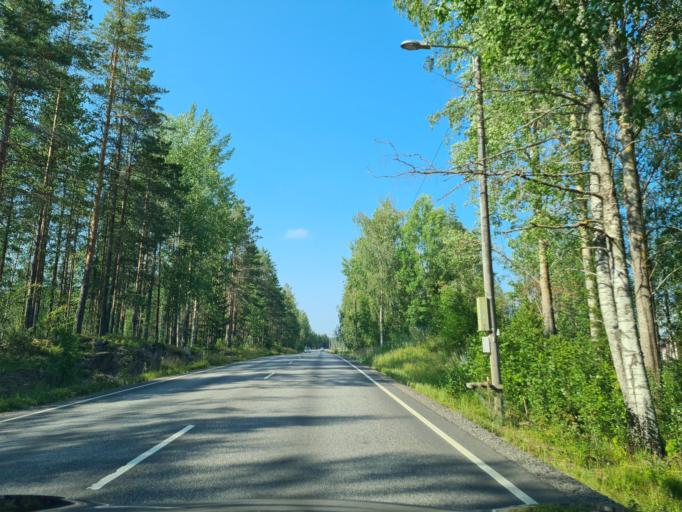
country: FI
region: Satakunta
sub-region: Pohjois-Satakunta
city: Kankaanpaeae
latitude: 61.9491
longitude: 22.5131
